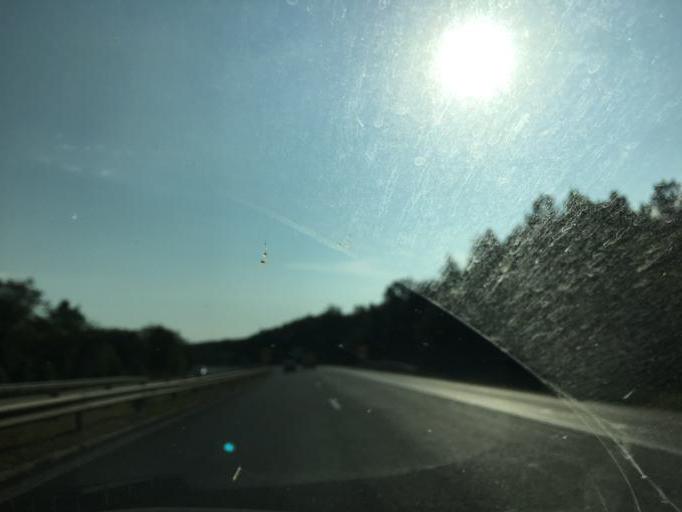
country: BG
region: Sofiya
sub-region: Obshtina Elin Pelin
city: Elin Pelin
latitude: 42.5927
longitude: 23.6039
